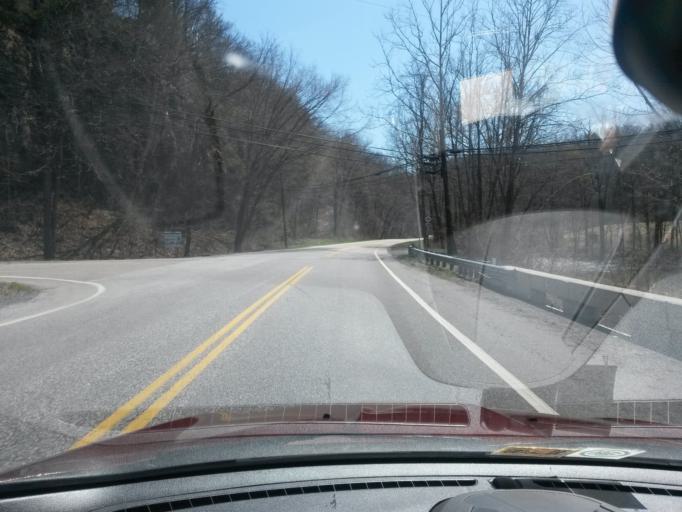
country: US
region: Virginia
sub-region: City of Covington
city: Covington
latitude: 37.8119
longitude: -80.0714
